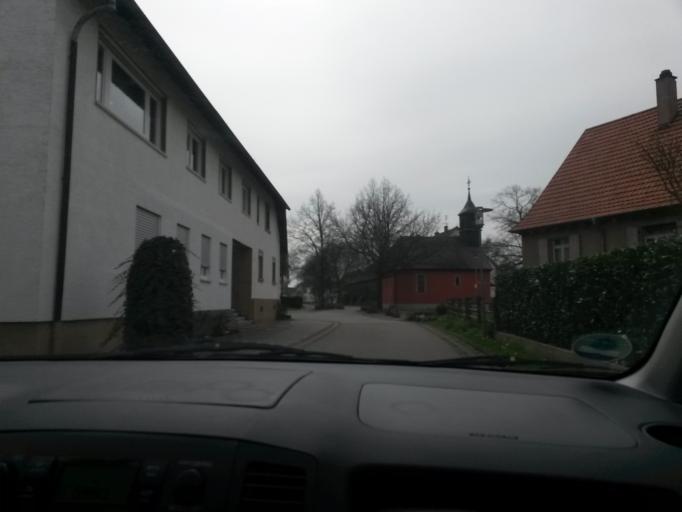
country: DE
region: Baden-Wuerttemberg
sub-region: Freiburg Region
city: Kippenheim
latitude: 48.3155
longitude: 7.8089
